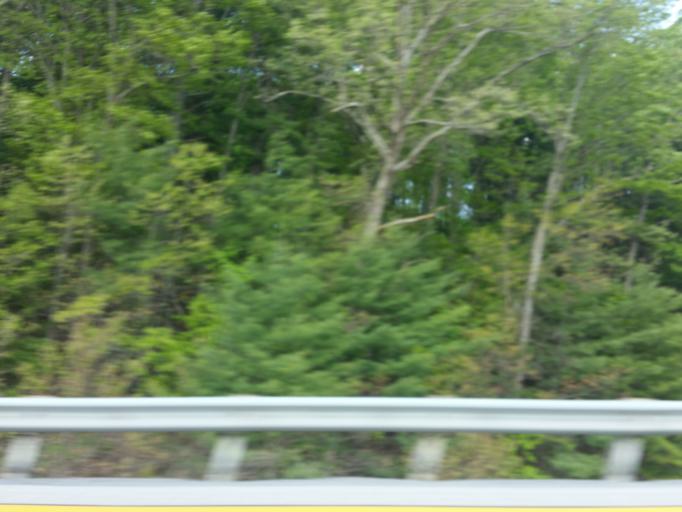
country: US
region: West Virginia
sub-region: Mercer County
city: Athens
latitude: 37.4120
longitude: -81.0634
